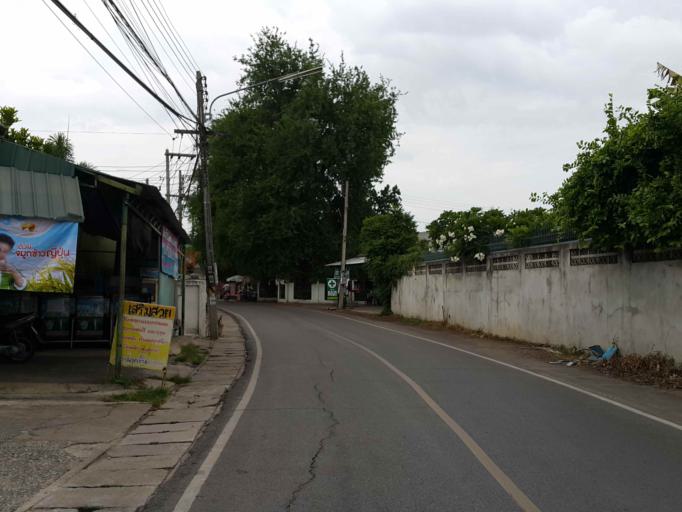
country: TH
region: Chiang Mai
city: Chiang Mai
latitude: 18.7528
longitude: 99.0005
